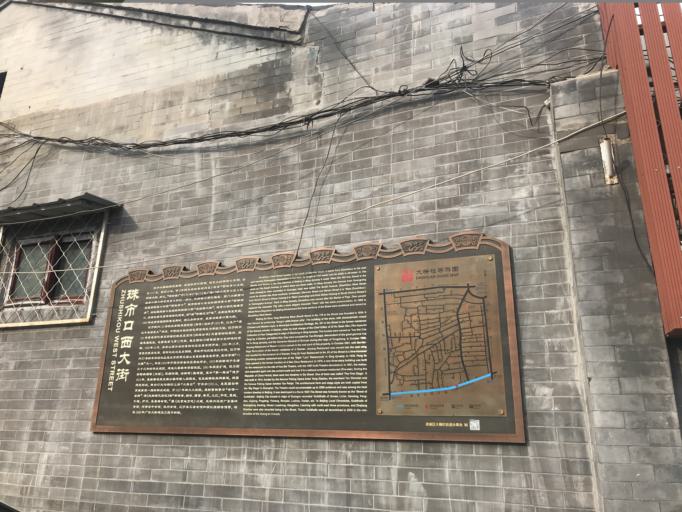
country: CN
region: Beijing
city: Beijing
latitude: 39.8890
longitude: 116.3872
